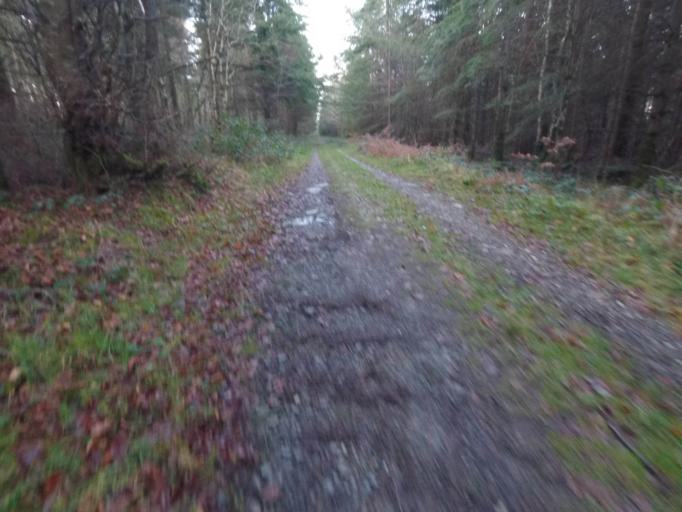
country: IE
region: Munster
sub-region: Waterford
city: Portlaw
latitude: 52.3017
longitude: -7.3427
